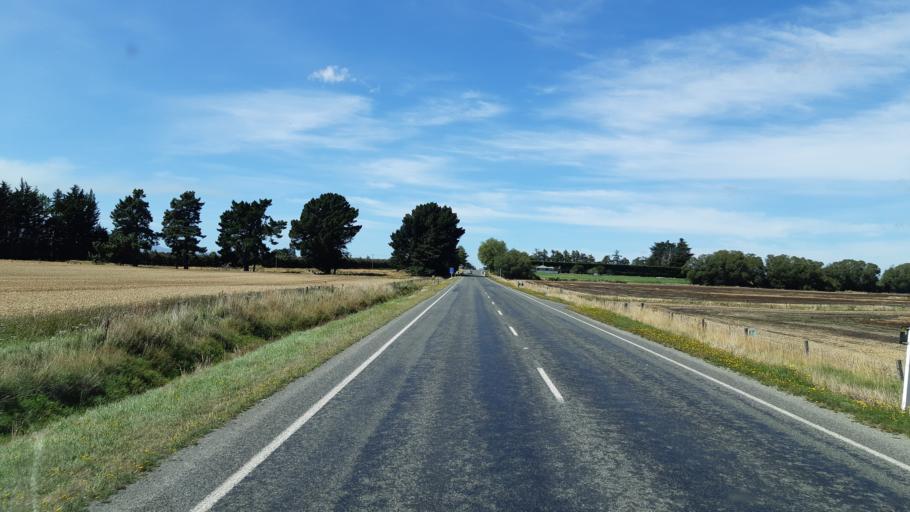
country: NZ
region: Southland
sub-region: Southland District
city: Winton
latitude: -45.8374
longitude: 168.5928
